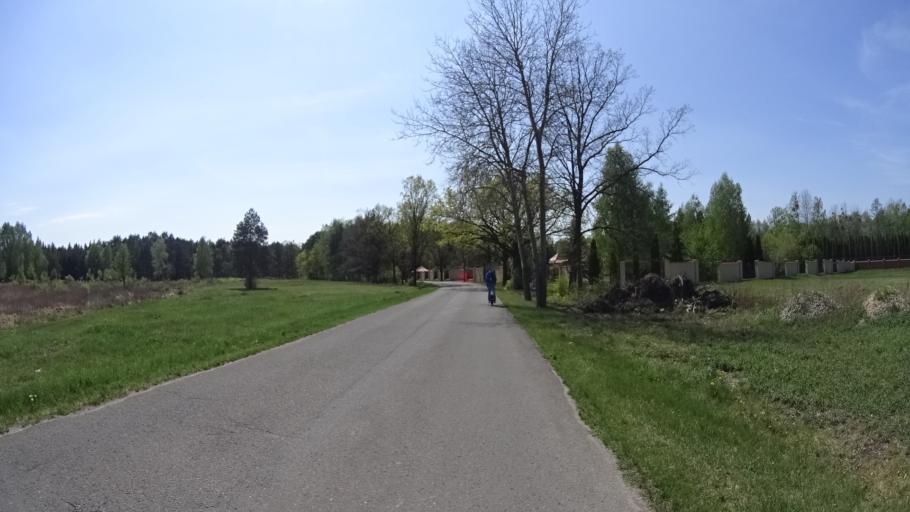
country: PL
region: Masovian Voivodeship
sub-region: Powiat warszawski zachodni
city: Truskaw
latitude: 52.2819
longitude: 20.7268
